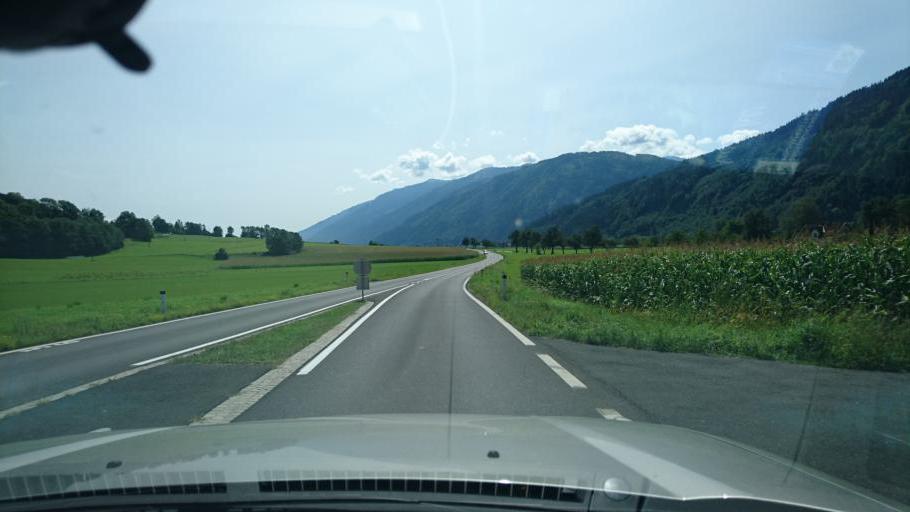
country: AT
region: Carinthia
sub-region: Politischer Bezirk Spittal an der Drau
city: Muhldorf
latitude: 46.8550
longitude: 13.3533
